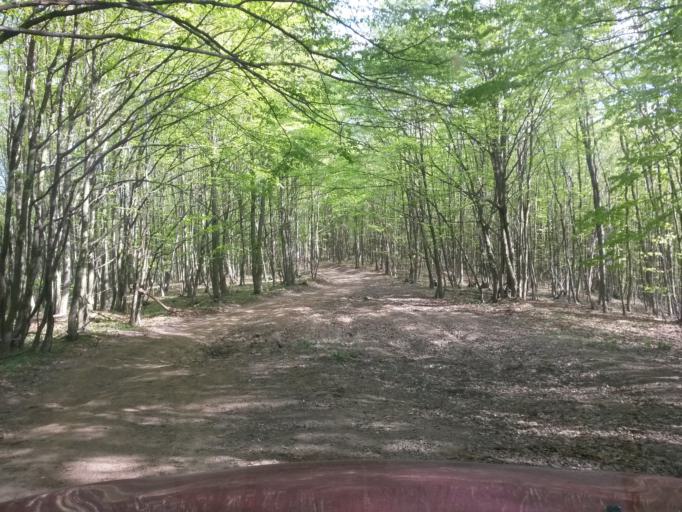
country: SK
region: Presovsky
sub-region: Okres Presov
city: Presov
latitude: 48.9518
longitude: 21.1343
